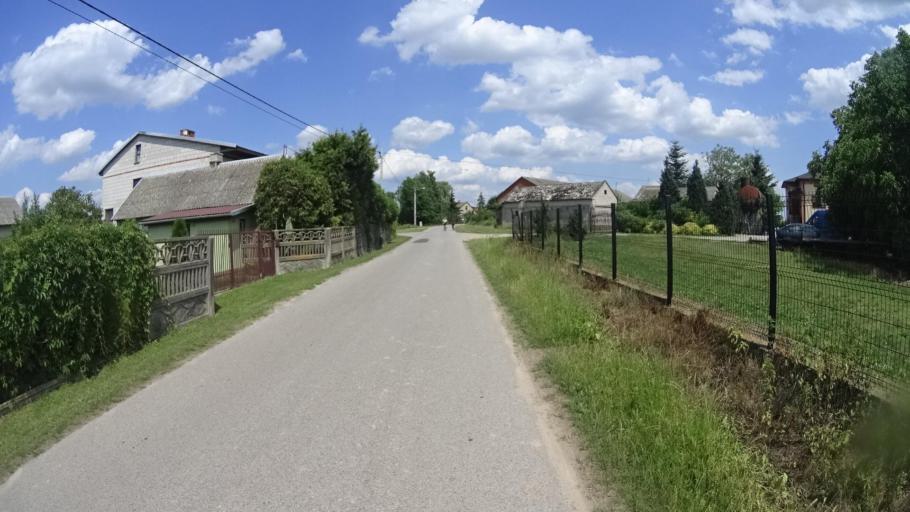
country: PL
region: Masovian Voivodeship
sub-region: Powiat bialobrzeski
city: Promna
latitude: 51.7036
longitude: 20.9222
